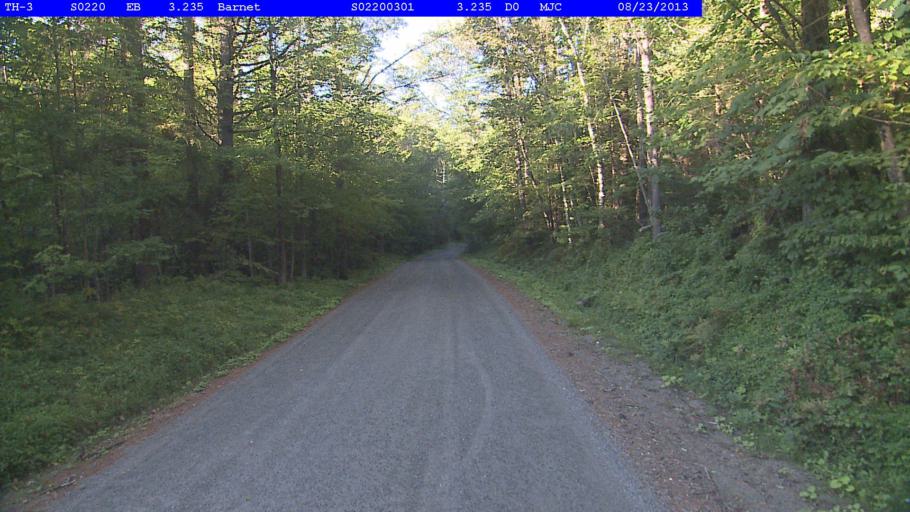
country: US
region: Vermont
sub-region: Caledonia County
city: Saint Johnsbury
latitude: 44.3404
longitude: -71.9961
